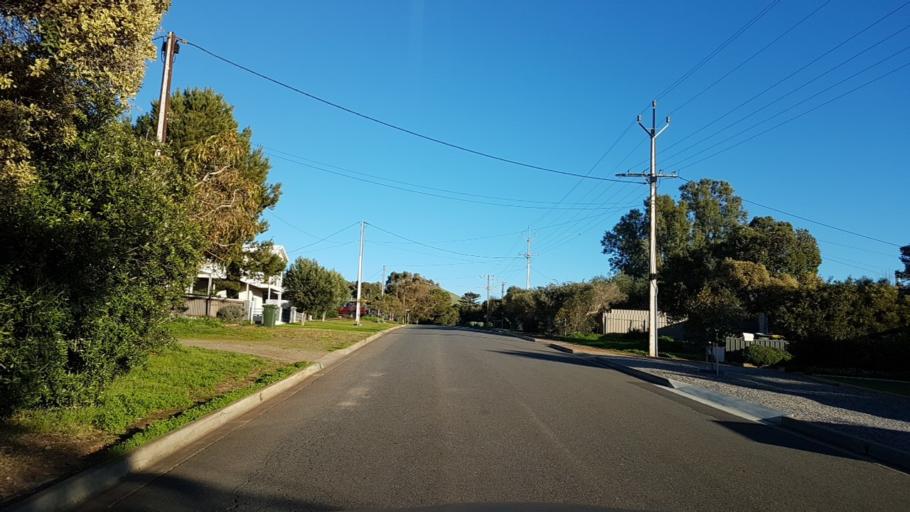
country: AU
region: South Australia
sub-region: Onkaparinga
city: Port Willunga
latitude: -35.3327
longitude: 138.4505
